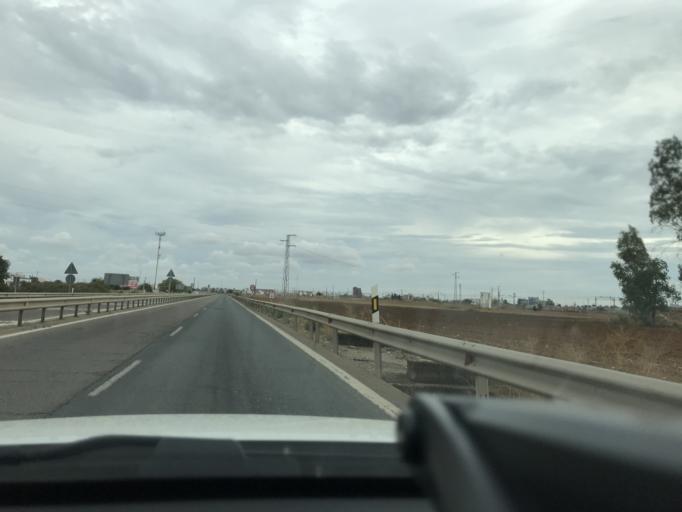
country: ES
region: Andalusia
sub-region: Provincia de Sevilla
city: Sevilla
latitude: 37.4218
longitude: -5.9475
